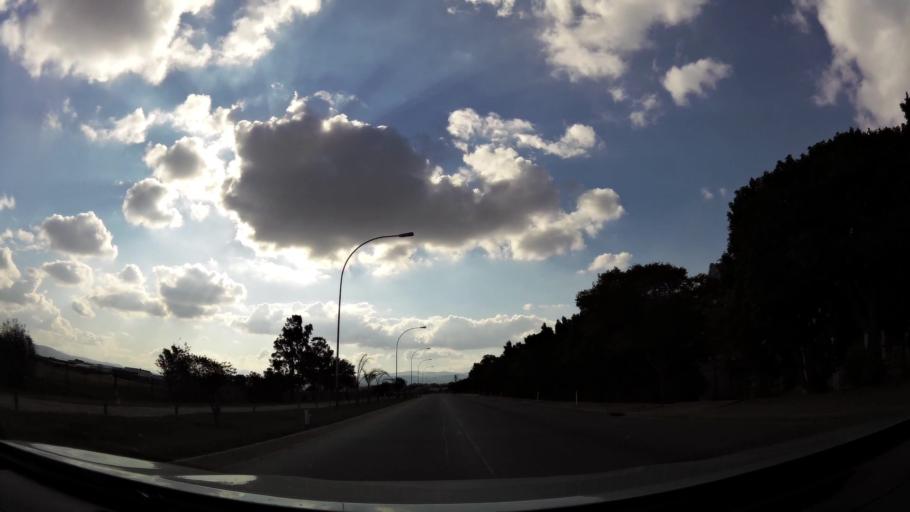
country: ZA
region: Eastern Cape
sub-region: Nelson Mandela Bay Metropolitan Municipality
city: Uitenhage
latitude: -33.7771
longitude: 25.3918
